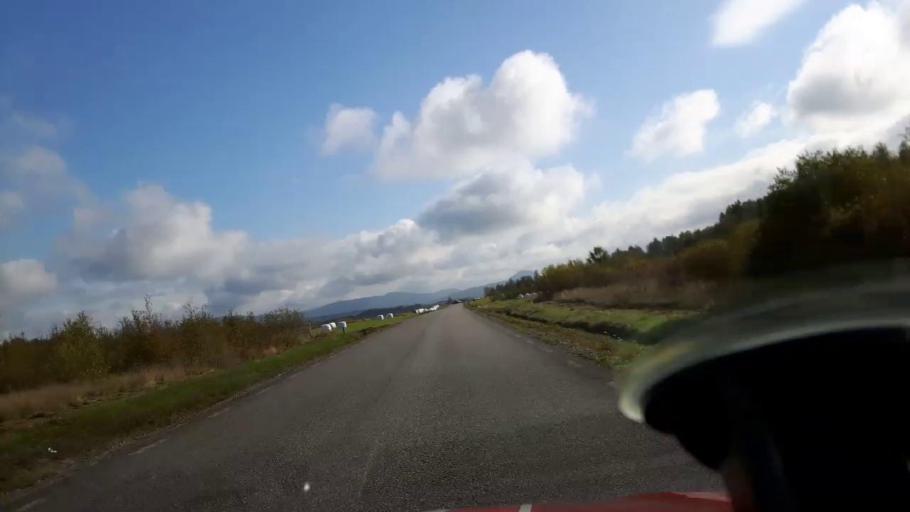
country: SE
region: Gaevleborg
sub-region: Ljusdals Kommun
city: Ljusdal
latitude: 61.7634
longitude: 16.0652
